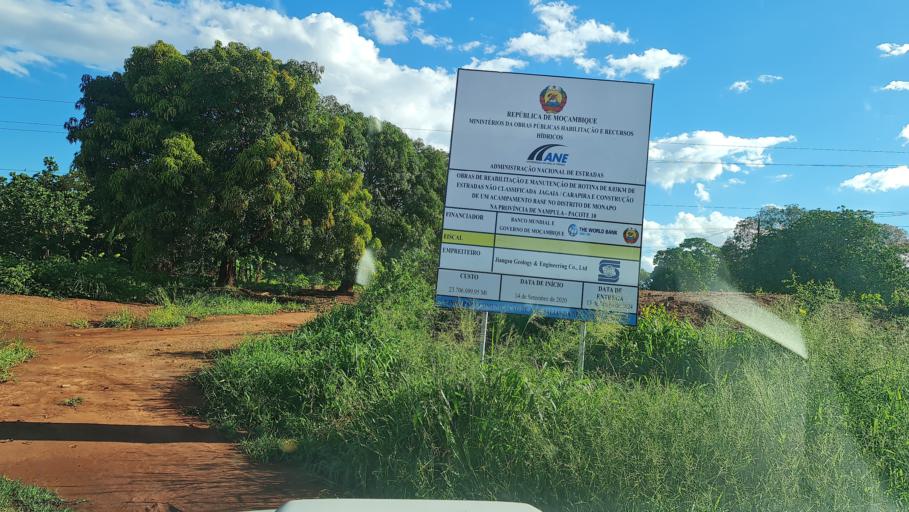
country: MZ
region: Nampula
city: Ilha de Mocambique
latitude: -14.9146
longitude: 40.2170
